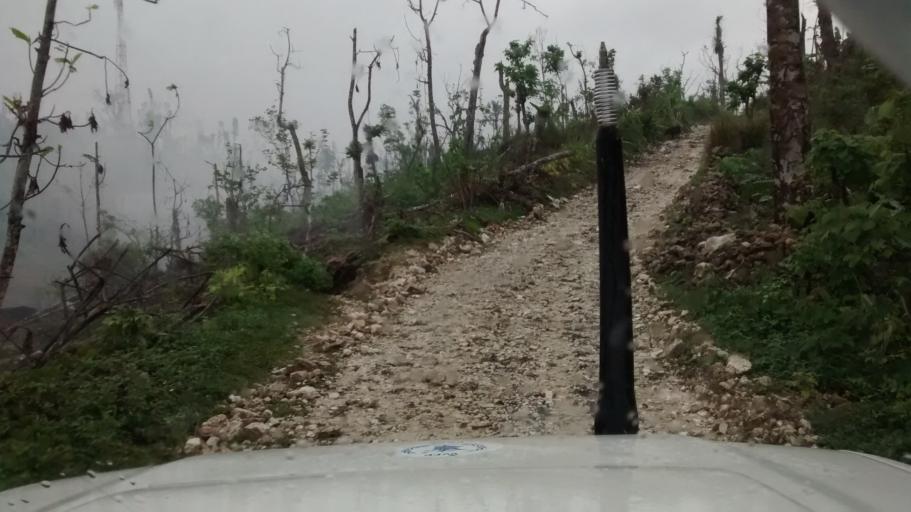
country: HT
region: Grandans
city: Moron
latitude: 18.5378
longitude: -74.1602
